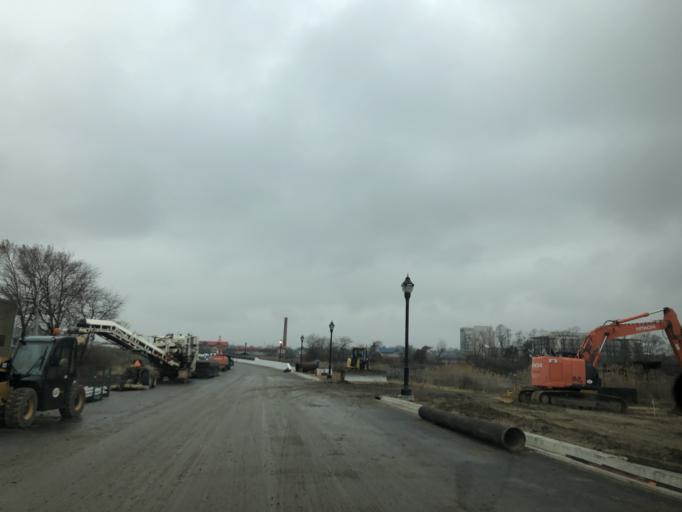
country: US
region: Delaware
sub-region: New Castle County
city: Wilmington
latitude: 39.7283
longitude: -75.5579
